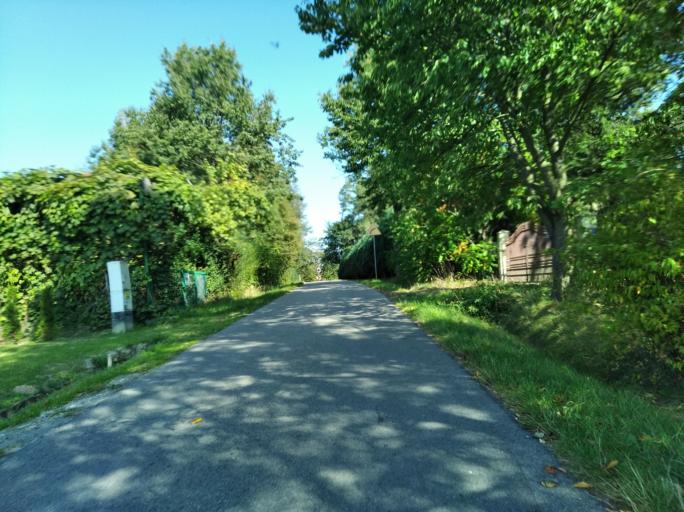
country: PL
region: Subcarpathian Voivodeship
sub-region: Powiat strzyzowski
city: Czudec
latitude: 49.9687
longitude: 21.8139
